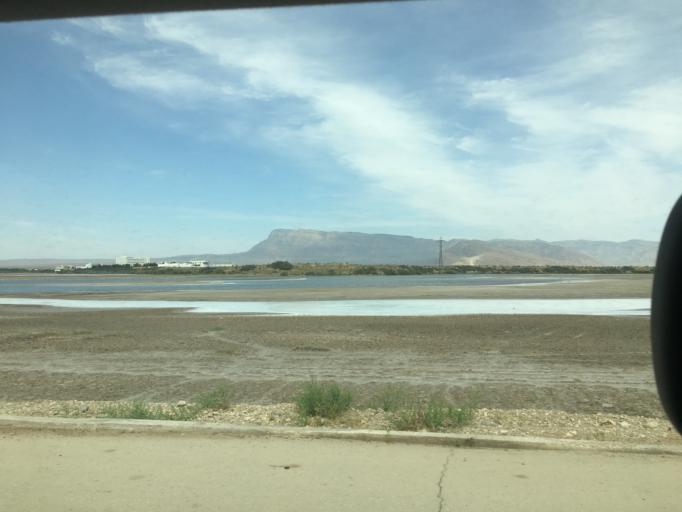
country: TM
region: Balkan
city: Balkanabat
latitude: 39.6196
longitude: 54.1630
